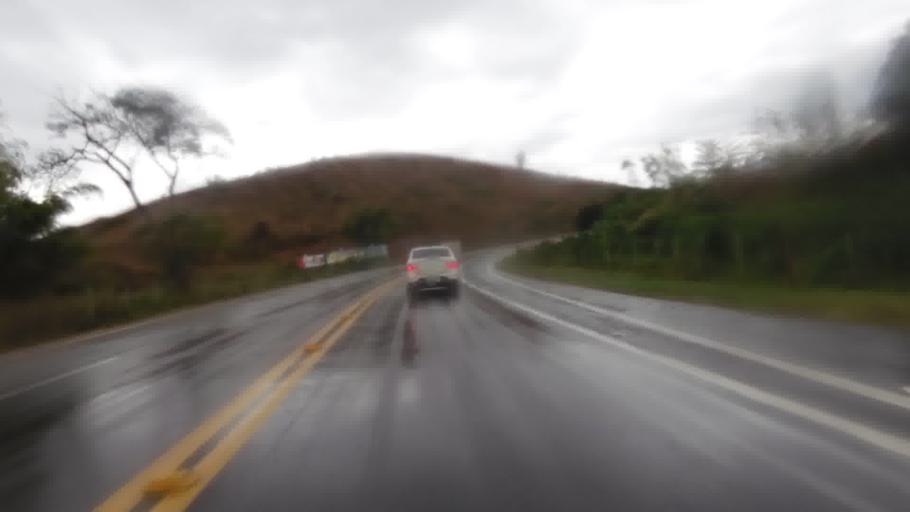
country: BR
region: Espirito Santo
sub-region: Cachoeiro De Itapemirim
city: Cachoeiro de Itapemirim
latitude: -20.9761
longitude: -41.1113
